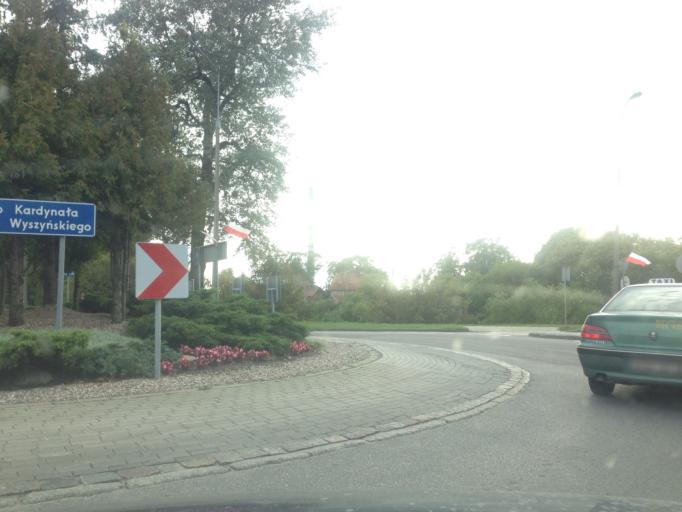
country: PL
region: Pomeranian Voivodeship
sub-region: Powiat kwidzynski
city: Kwidzyn
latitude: 53.7264
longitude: 18.9324
